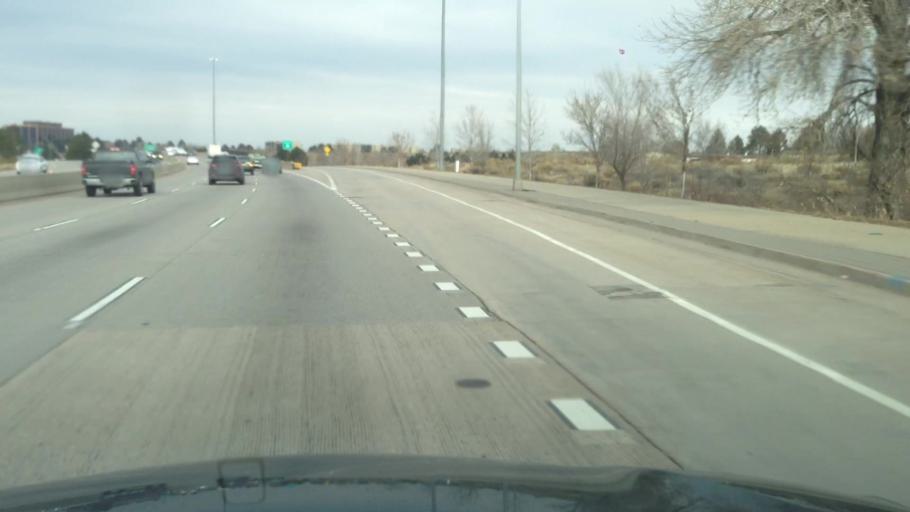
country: US
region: Colorado
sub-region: Arapahoe County
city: Dove Valley
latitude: 39.6497
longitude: -104.8298
